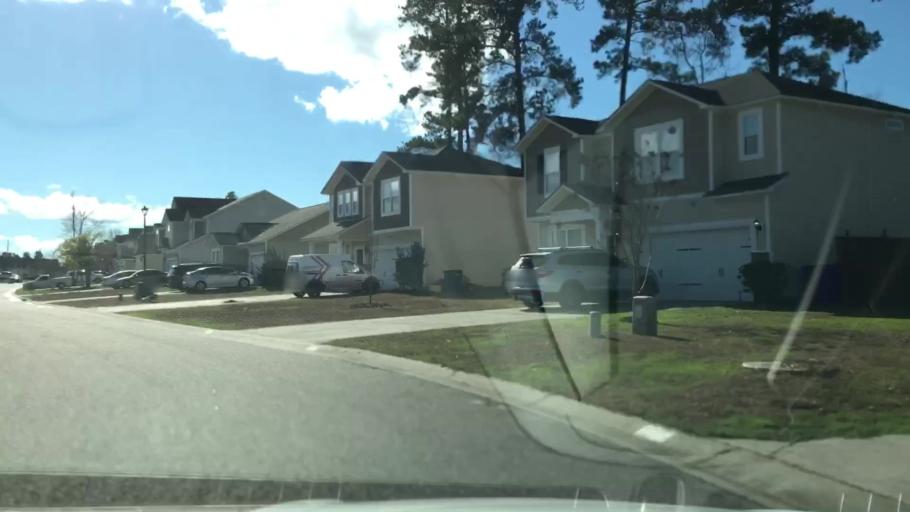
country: US
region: South Carolina
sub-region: Dorchester County
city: Summerville
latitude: 33.0913
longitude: -80.1971
